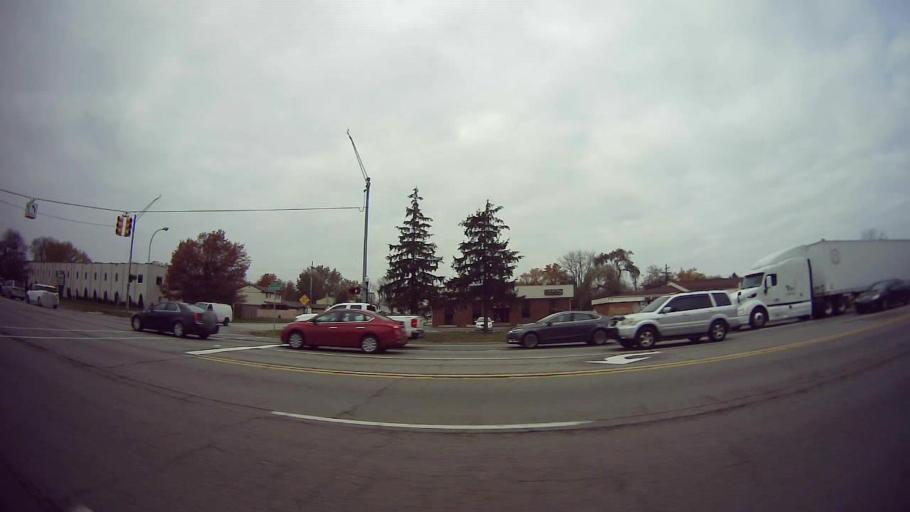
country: US
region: Michigan
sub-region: Oakland County
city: Southfield
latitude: 42.4810
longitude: -83.2212
